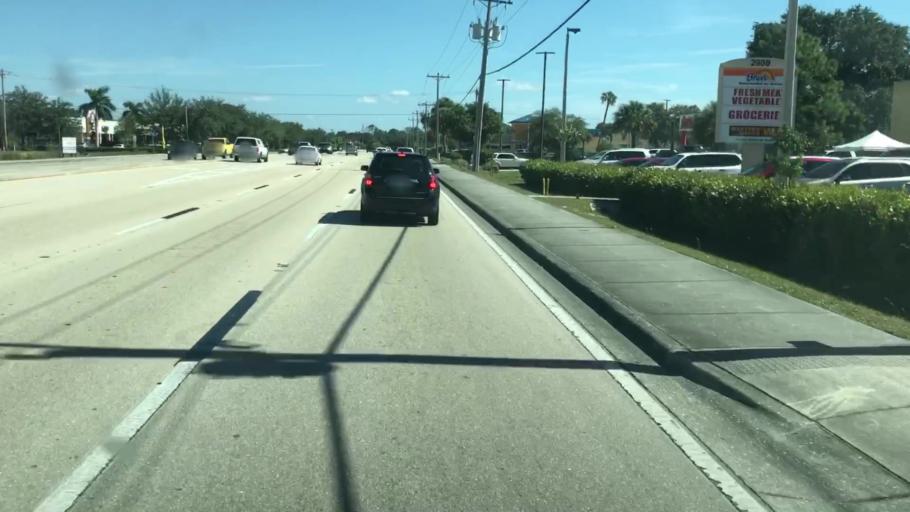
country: US
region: Florida
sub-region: Lee County
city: Lehigh Acres
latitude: 26.6172
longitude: -81.6743
